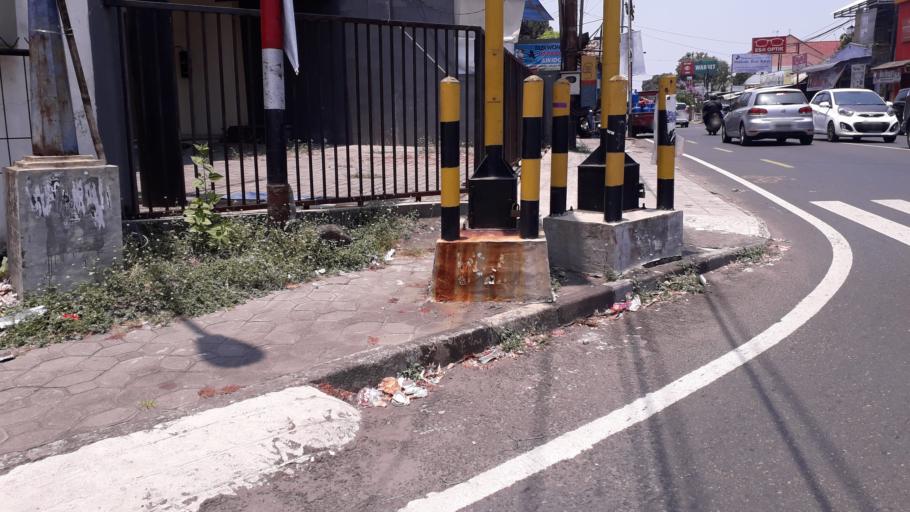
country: ID
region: Daerah Istimewa Yogyakarta
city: Yogyakarta
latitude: -7.7621
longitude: 110.3694
